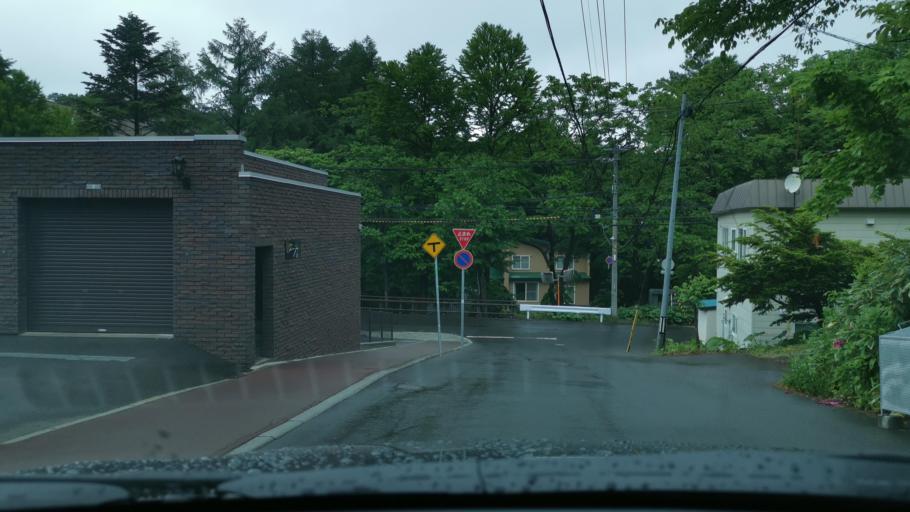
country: JP
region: Hokkaido
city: Sapporo
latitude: 43.0453
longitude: 141.3081
